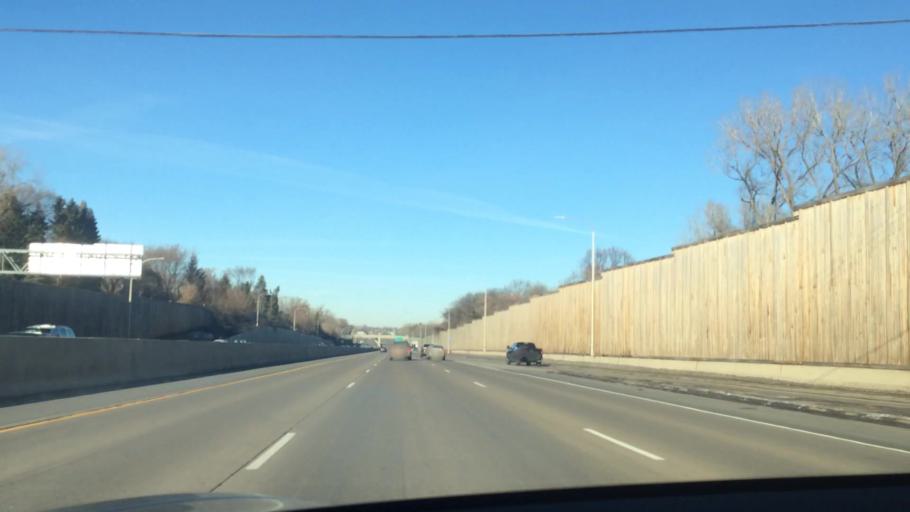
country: US
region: Minnesota
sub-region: Hennepin County
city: Golden Valley
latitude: 45.0027
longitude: -93.3516
